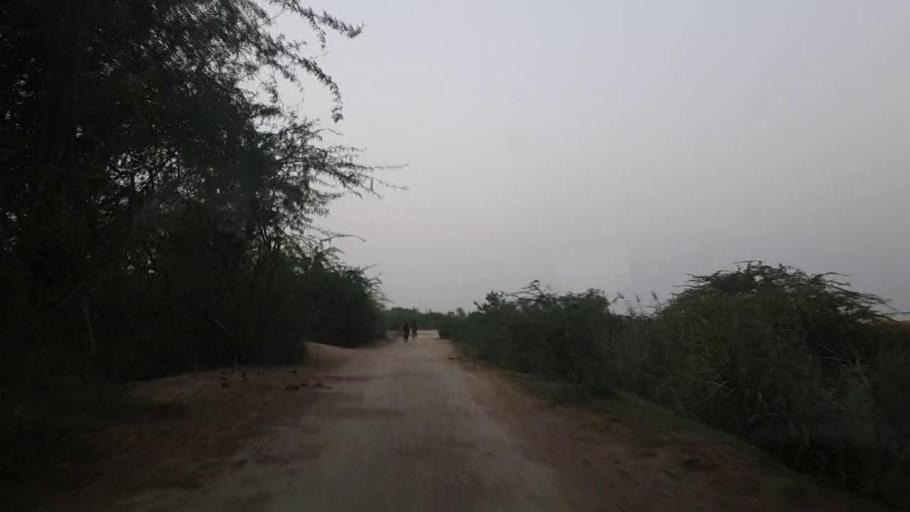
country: PK
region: Sindh
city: Mirpur Sakro
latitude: 24.5852
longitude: 67.7842
